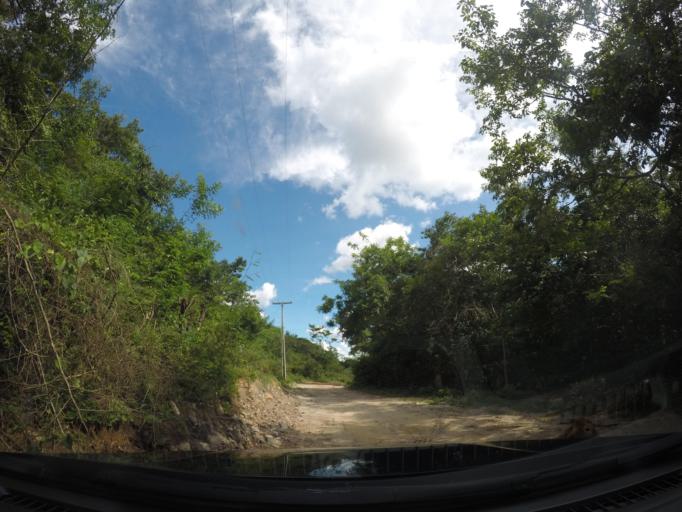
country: BR
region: Bahia
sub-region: Barra Da Estiva
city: Barra da Estiva
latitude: -13.1535
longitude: -41.5946
